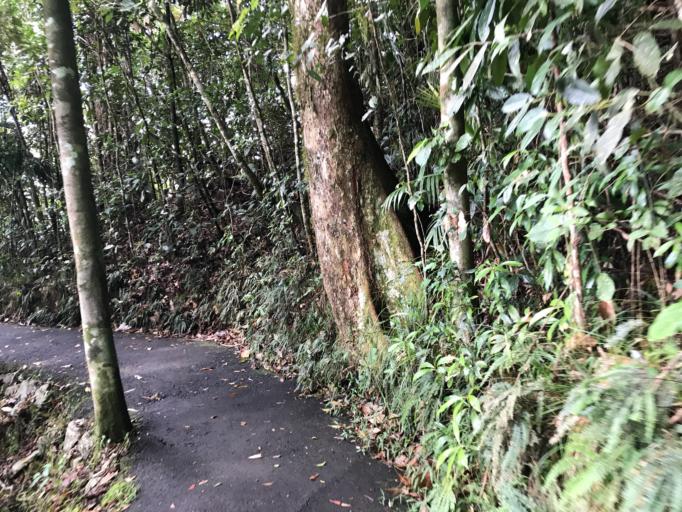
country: AU
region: Queensland
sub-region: Mackay
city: Walkerston
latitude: -21.1448
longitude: 148.4997
